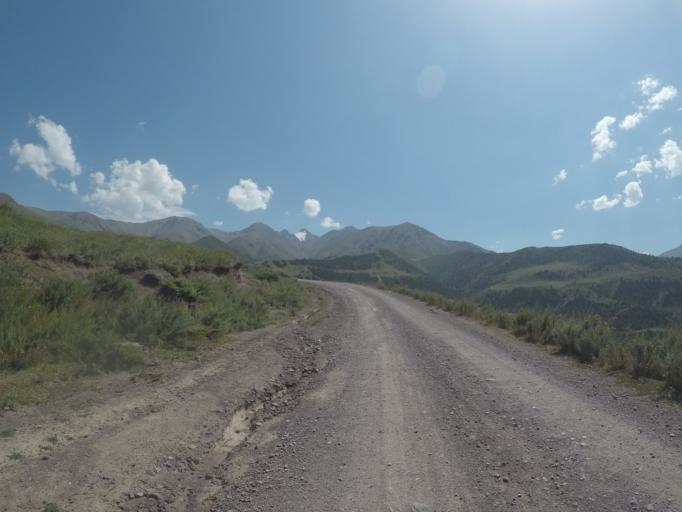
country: KG
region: Chuy
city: Bishkek
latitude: 42.6479
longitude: 74.5214
